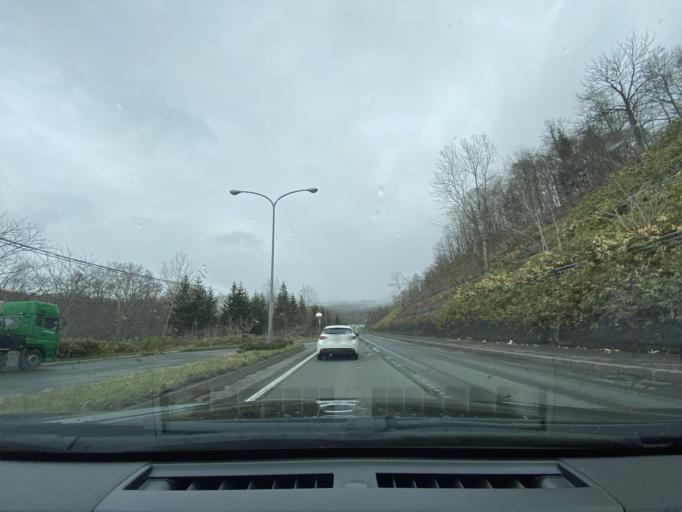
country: JP
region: Hokkaido
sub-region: Asahikawa-shi
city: Asahikawa
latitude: 43.7533
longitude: 142.2582
